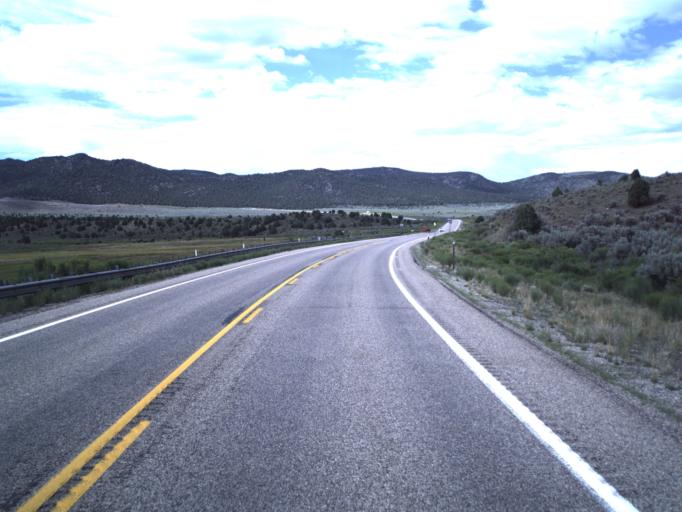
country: US
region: Utah
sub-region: Garfield County
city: Panguitch
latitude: 38.0019
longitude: -112.5094
